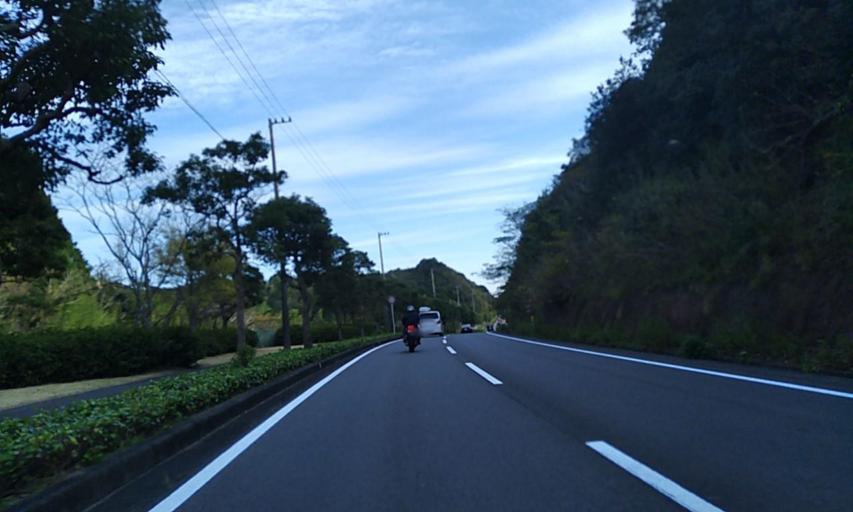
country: JP
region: Mie
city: Toba
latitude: 34.3592
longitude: 136.8036
